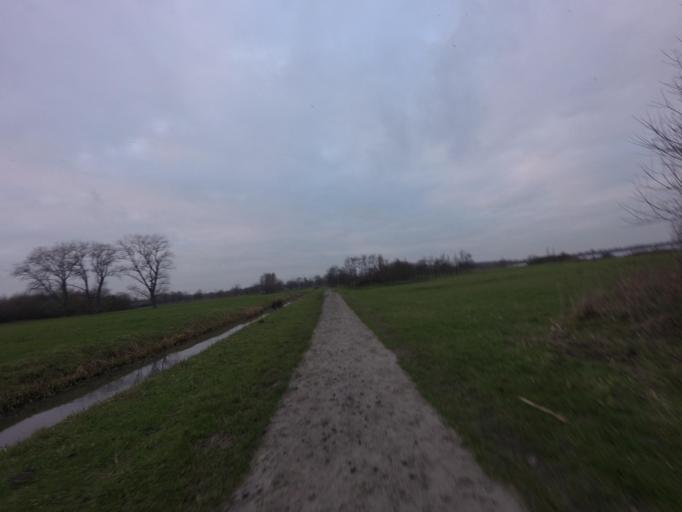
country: NL
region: Utrecht
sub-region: Stichtse Vecht
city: Spechtenkamp
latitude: 52.1183
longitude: 5.0114
